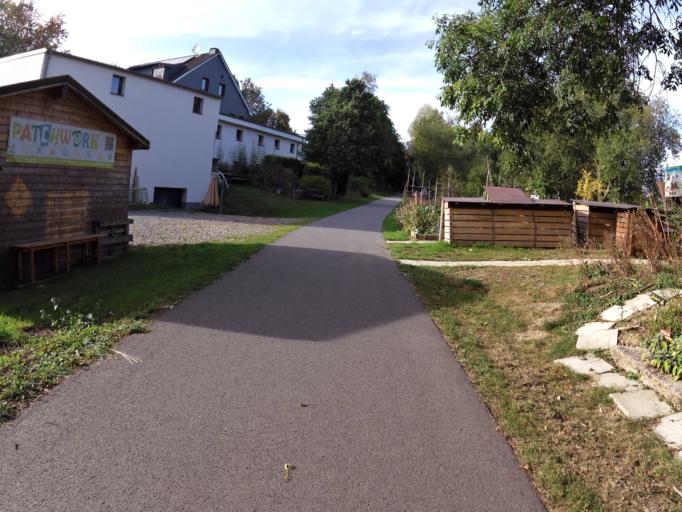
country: BE
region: Wallonia
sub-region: Province de Liege
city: Saint-Vith
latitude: 50.2765
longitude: 6.1325
